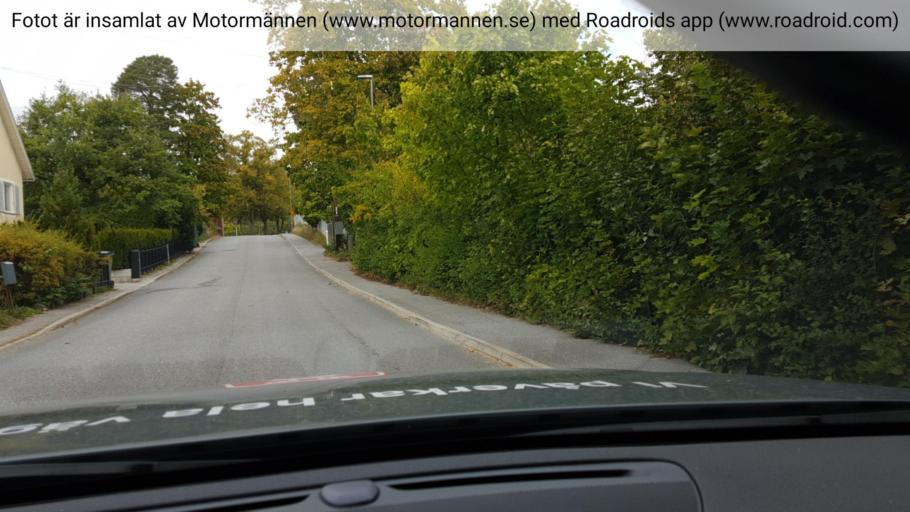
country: SE
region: Stockholm
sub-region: Danderyds Kommun
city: Djursholm
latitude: 59.3843
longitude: 18.0610
